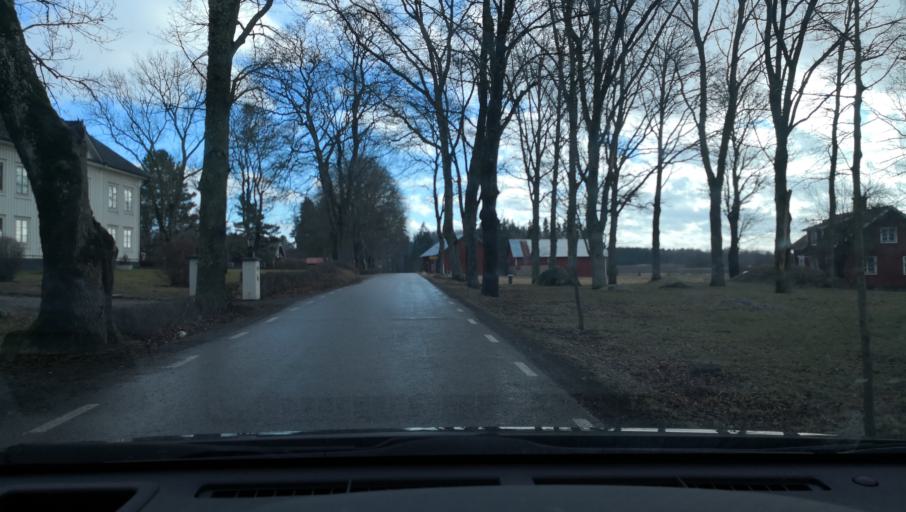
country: SE
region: OErebro
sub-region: Lindesbergs Kommun
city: Fellingsbro
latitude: 59.3466
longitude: 15.6862
